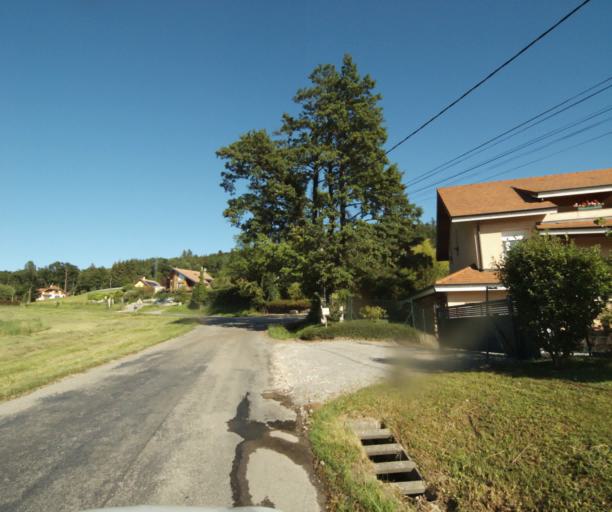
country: FR
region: Rhone-Alpes
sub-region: Departement de la Haute-Savoie
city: Massongy
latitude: 46.3136
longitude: 6.3415
